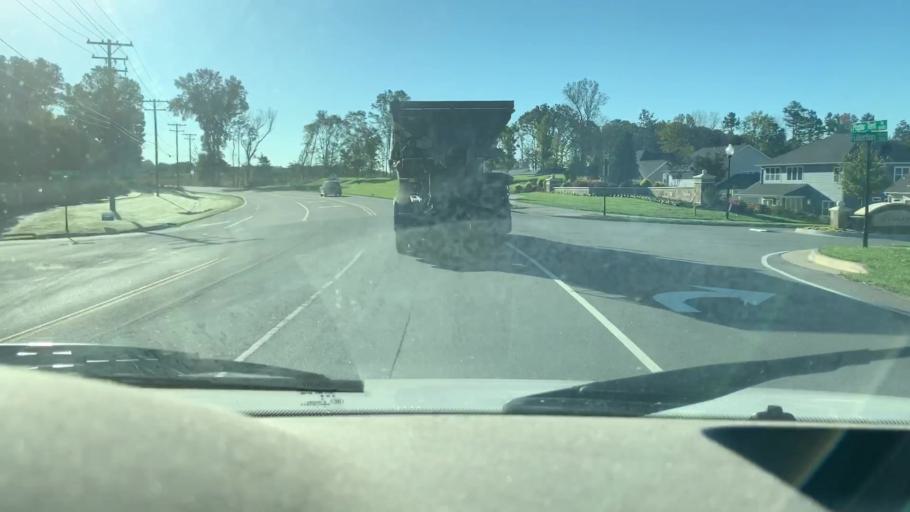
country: US
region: North Carolina
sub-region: Mecklenburg County
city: Huntersville
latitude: 35.4212
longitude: -80.7533
